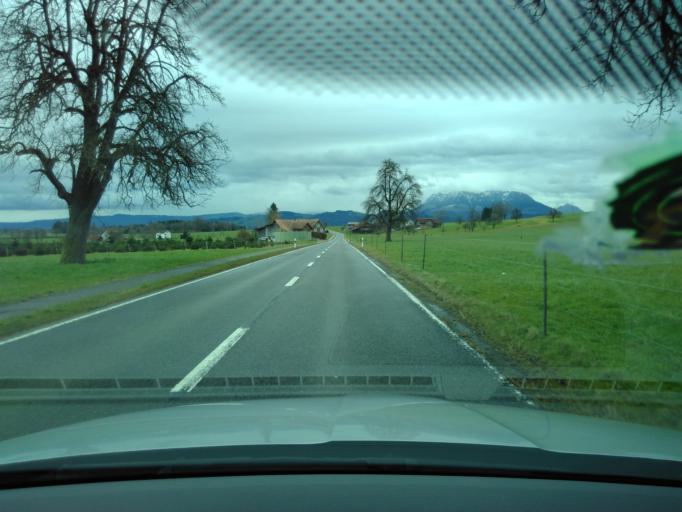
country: CH
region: Lucerne
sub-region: Hochdorf District
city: Hochdorf
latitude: 47.1309
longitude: 8.2813
